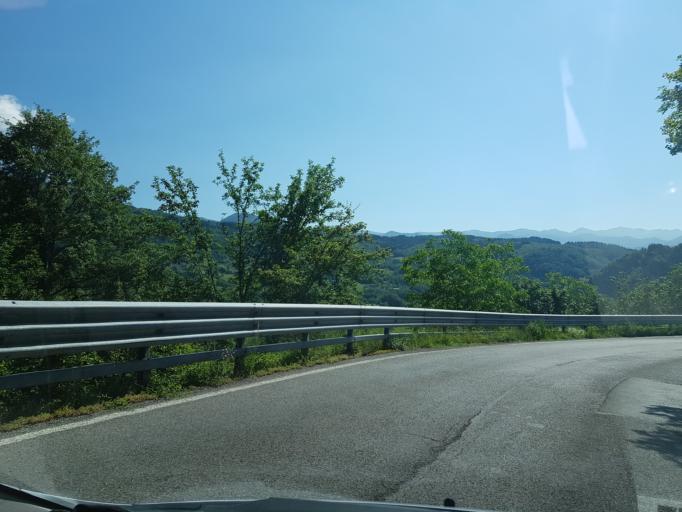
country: IT
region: Tuscany
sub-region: Provincia di Lucca
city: Camporgiano
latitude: 44.1540
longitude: 10.3420
